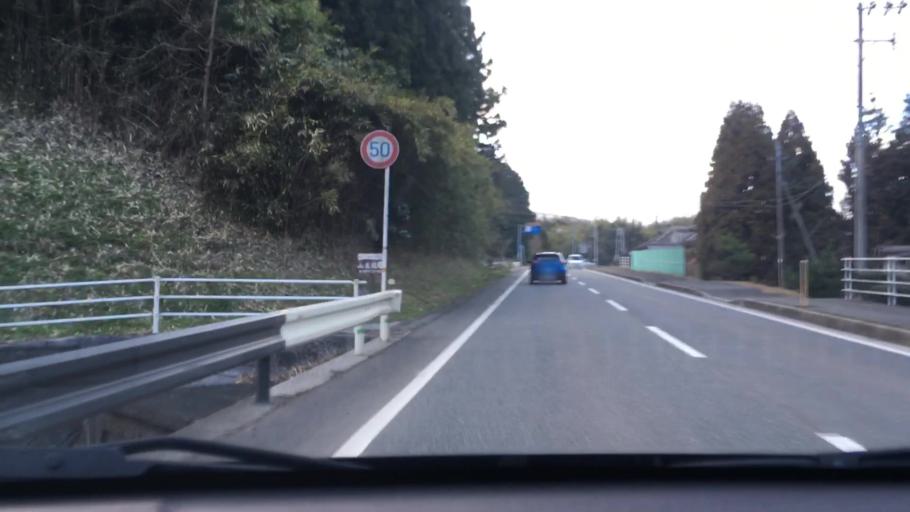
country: JP
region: Oita
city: Hiji
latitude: 33.3729
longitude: 131.4599
